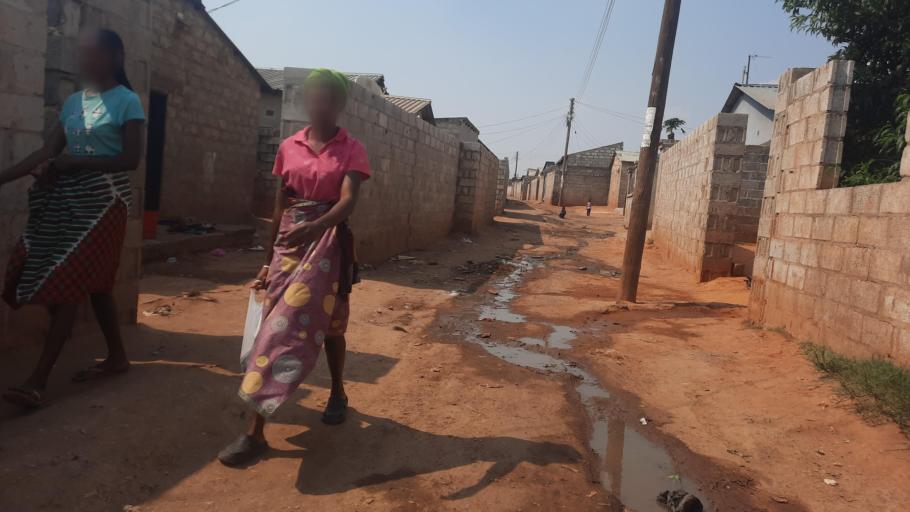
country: ZM
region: Lusaka
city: Lusaka
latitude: -15.4005
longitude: 28.3808
